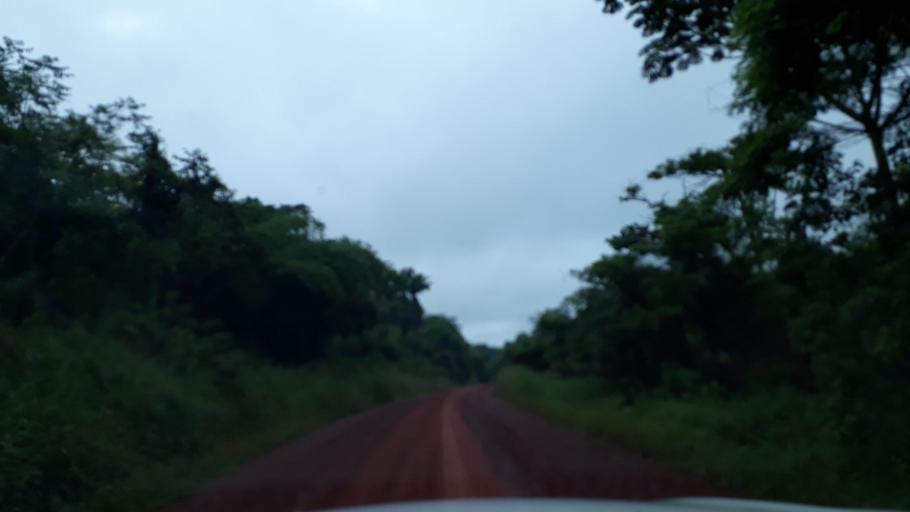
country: CD
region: Eastern Province
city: Wamba
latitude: 1.3521
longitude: 27.5908
